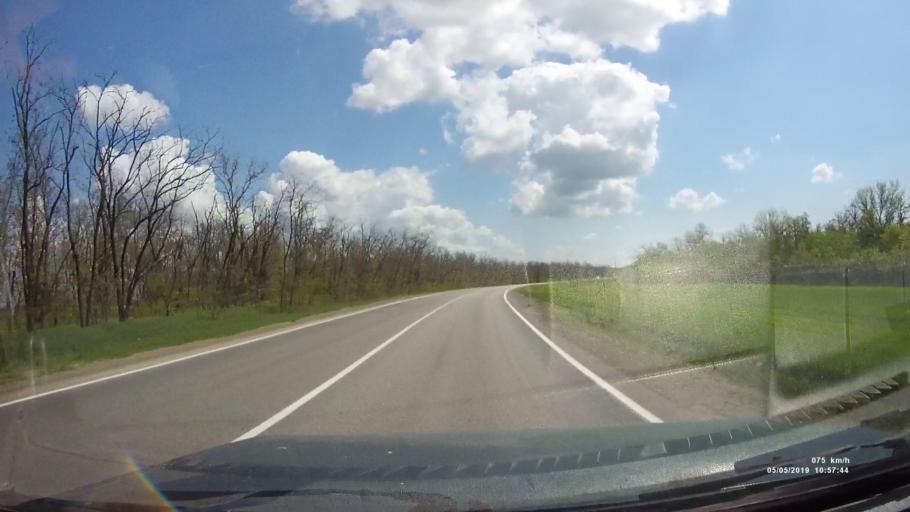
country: RU
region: Rostov
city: Ust'-Donetskiy
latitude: 47.6715
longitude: 40.8413
